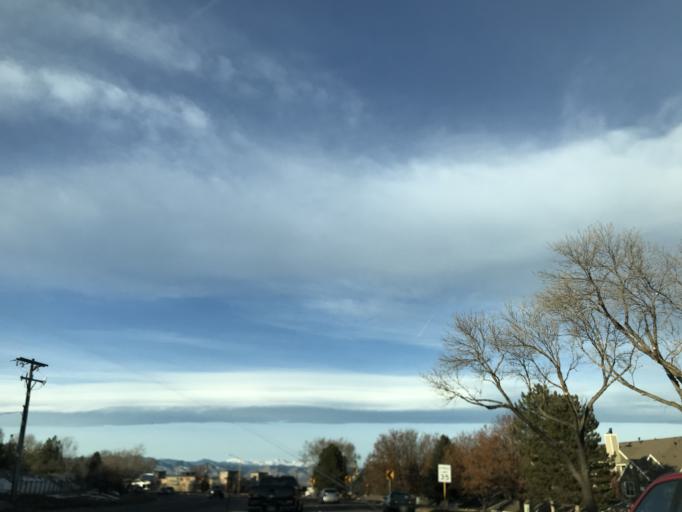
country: US
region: Colorado
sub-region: Arapahoe County
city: Cherry Hills Village
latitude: 39.6533
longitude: -104.9683
